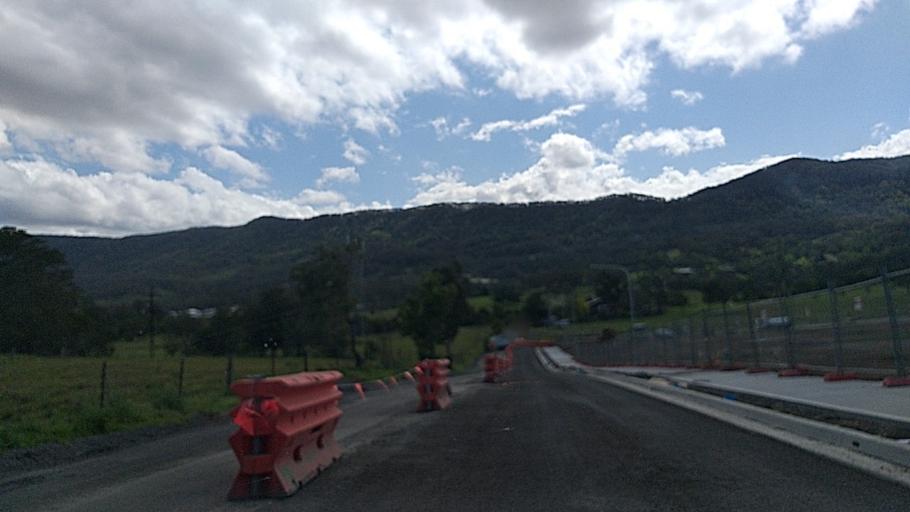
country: AU
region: New South Wales
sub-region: Wollongong
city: Dapto
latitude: -34.4704
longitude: 150.7732
